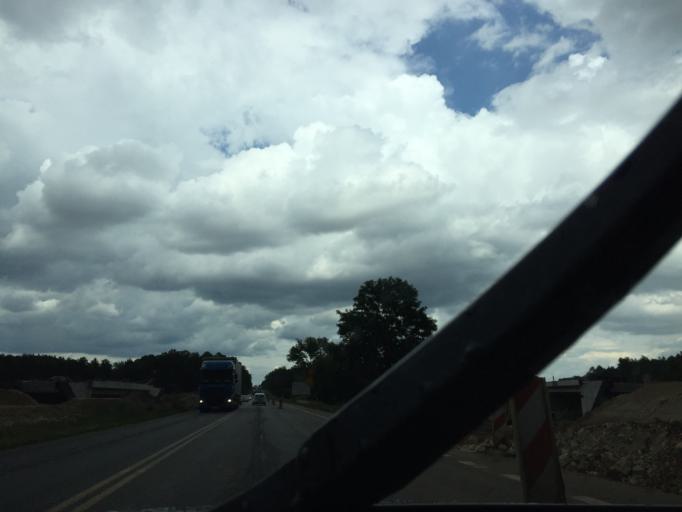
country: PL
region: Swietokrzyskie
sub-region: Powiat jedrzejowski
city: Jedrzejow
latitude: 50.6846
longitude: 20.3562
